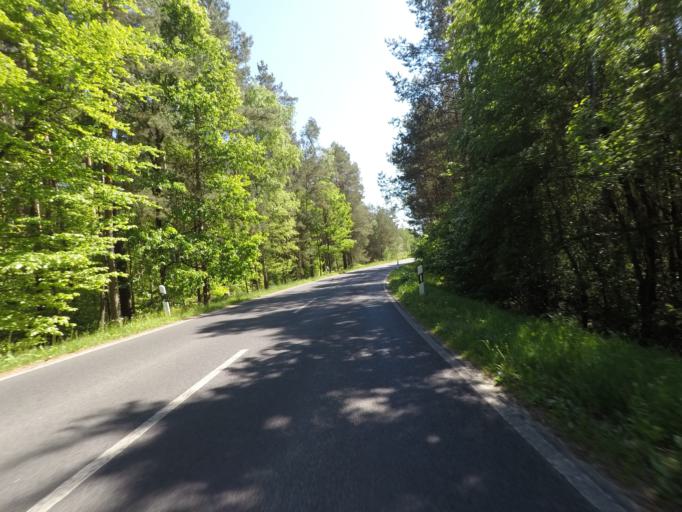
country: DE
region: Brandenburg
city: Eberswalde
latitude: 52.8262
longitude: 13.7702
